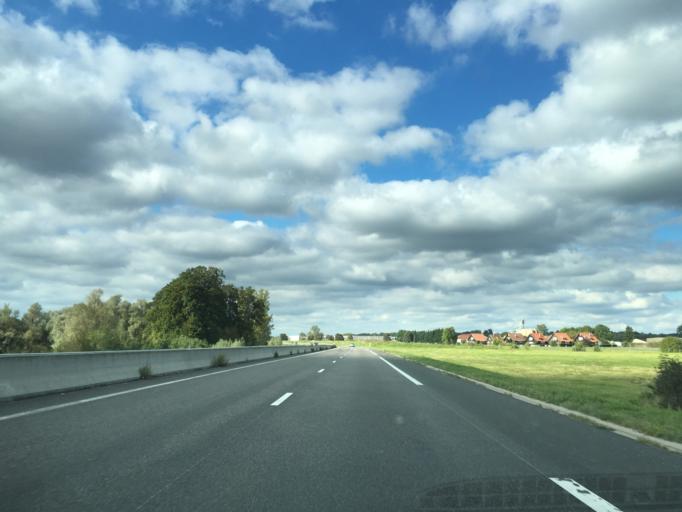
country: FR
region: Lorraine
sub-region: Departement de Meurthe-et-Moselle
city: Chanteheux
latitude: 48.5371
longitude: 6.5768
